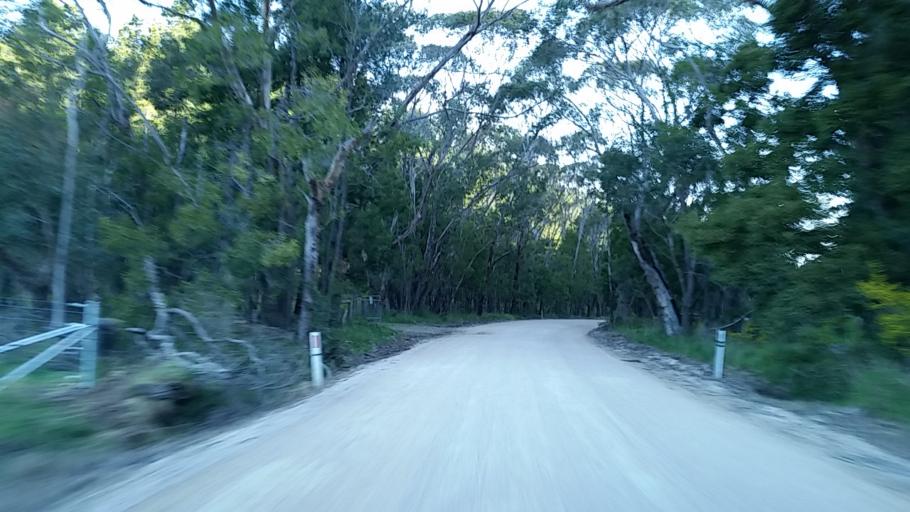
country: AU
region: South Australia
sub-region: Mount Barker
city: Meadows
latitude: -35.2542
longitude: 138.7067
